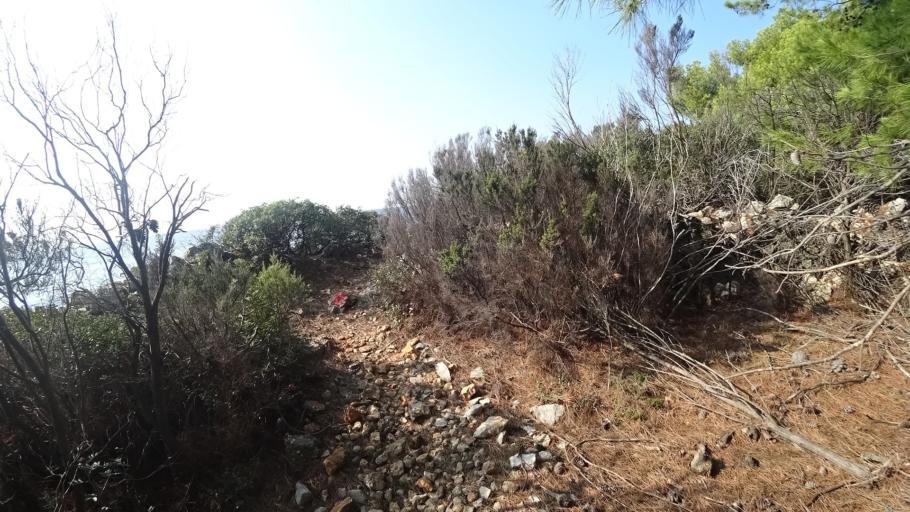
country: HR
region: Primorsko-Goranska
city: Mali Losinj
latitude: 44.4808
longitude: 14.5116
